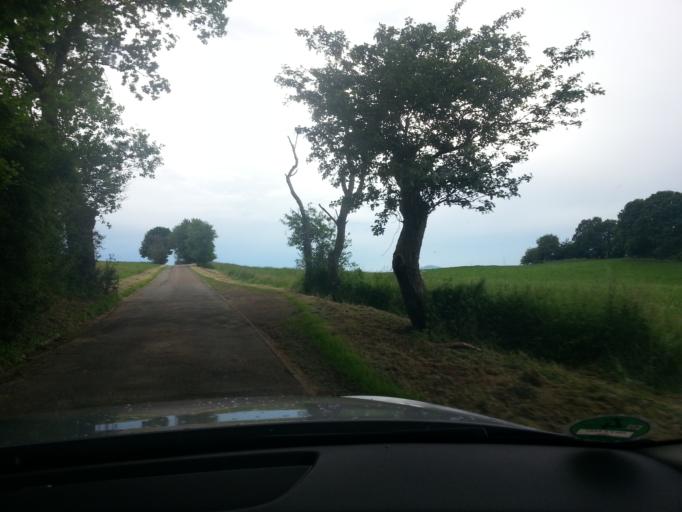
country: DE
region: Saarland
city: Sankt Wendel
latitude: 49.5037
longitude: 7.1849
